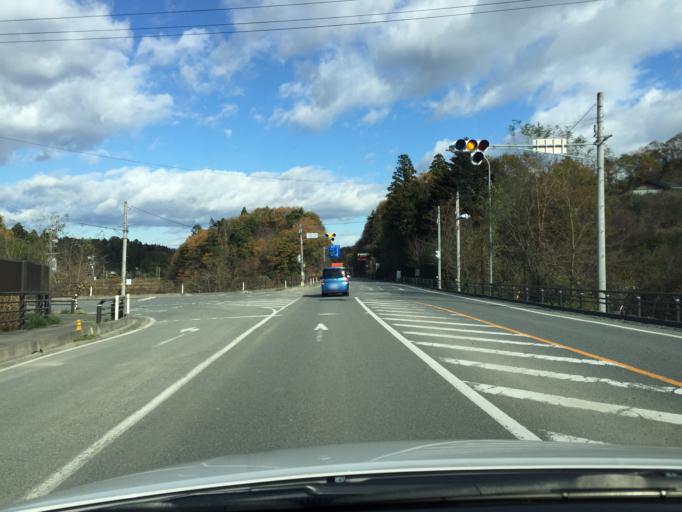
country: JP
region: Fukushima
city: Namie
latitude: 37.3677
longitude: 141.0089
